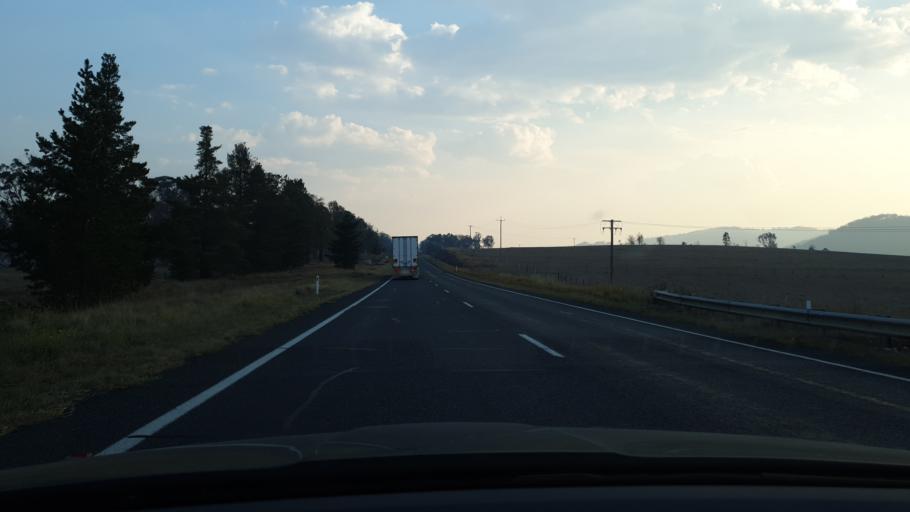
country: AU
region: New South Wales
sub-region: Tenterfield Municipality
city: Carrolls Creek
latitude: -29.0961
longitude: 152.0021
